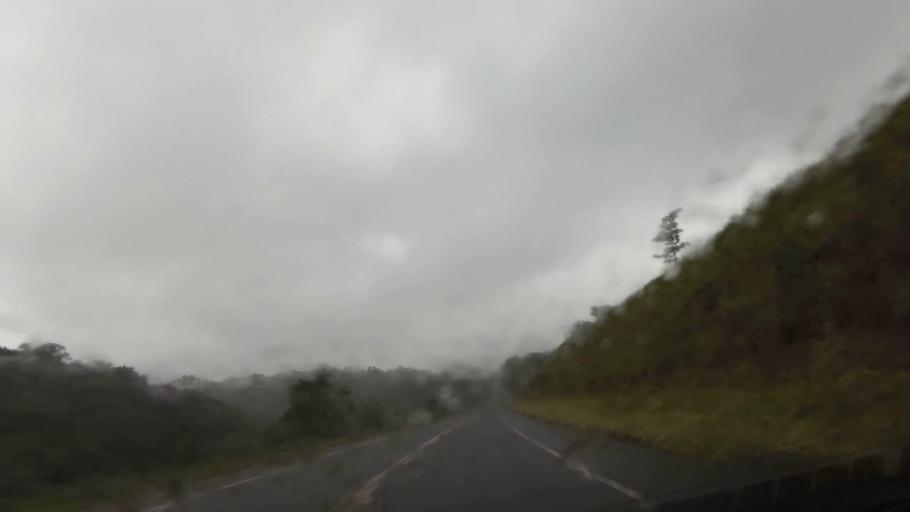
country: BR
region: Espirito Santo
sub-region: Guarapari
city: Guarapari
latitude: -20.6380
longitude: -40.5294
